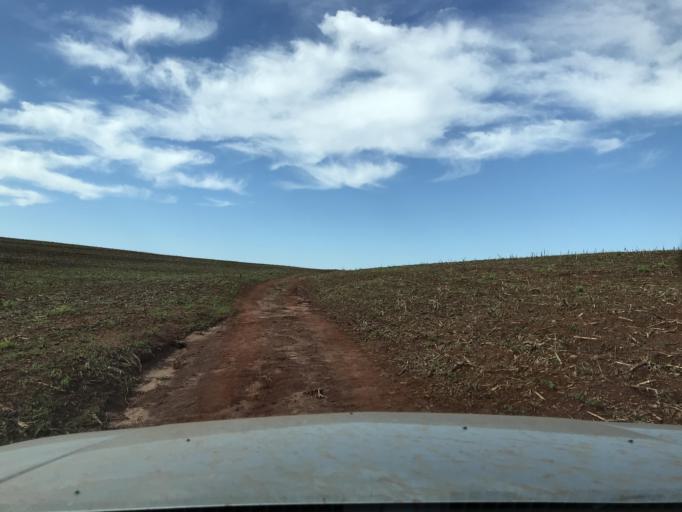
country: BR
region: Parana
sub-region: Palotina
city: Palotina
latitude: -24.1726
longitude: -53.8384
